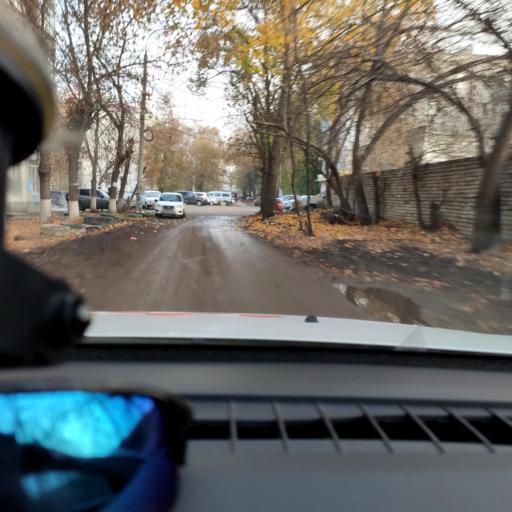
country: RU
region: Samara
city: Samara
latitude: 53.1923
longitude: 50.1880
